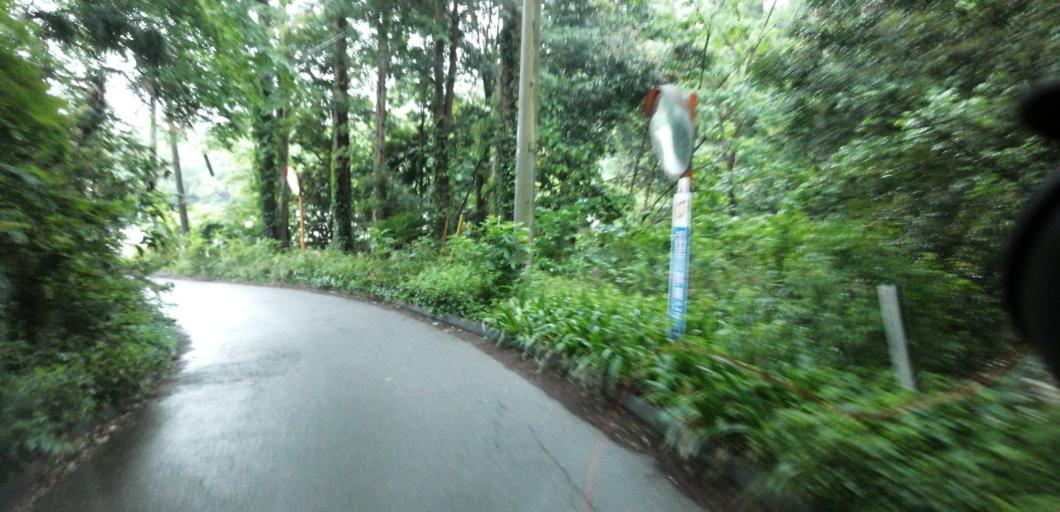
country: JP
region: Chiba
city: Yachimata
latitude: 35.5912
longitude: 140.2718
